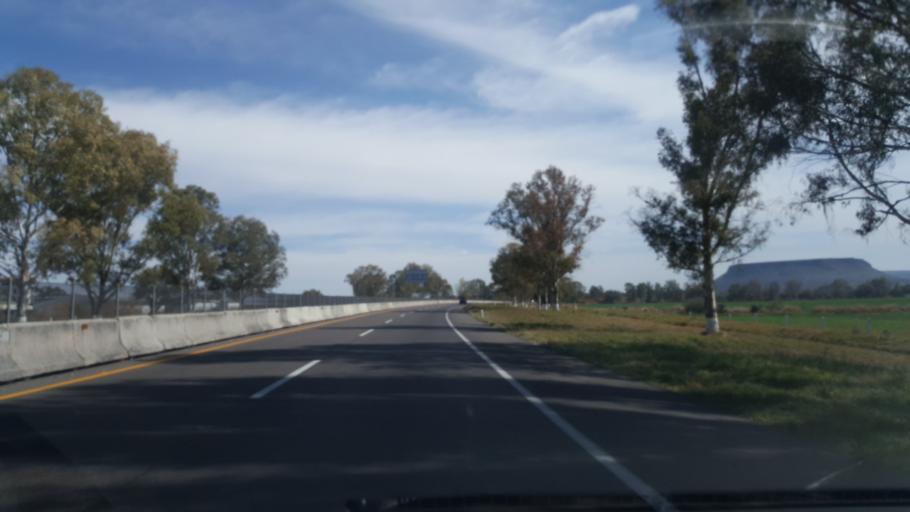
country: MX
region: Jalisco
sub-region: Lagos de Moreno
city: Cristeros [Fraccionamiento]
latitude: 21.3164
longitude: -102.0404
